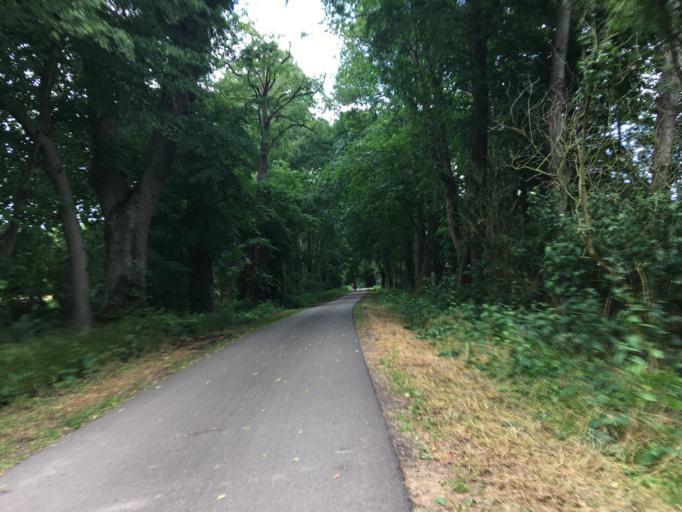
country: DE
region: Brandenburg
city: Althuttendorf
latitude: 53.0243
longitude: 13.8639
